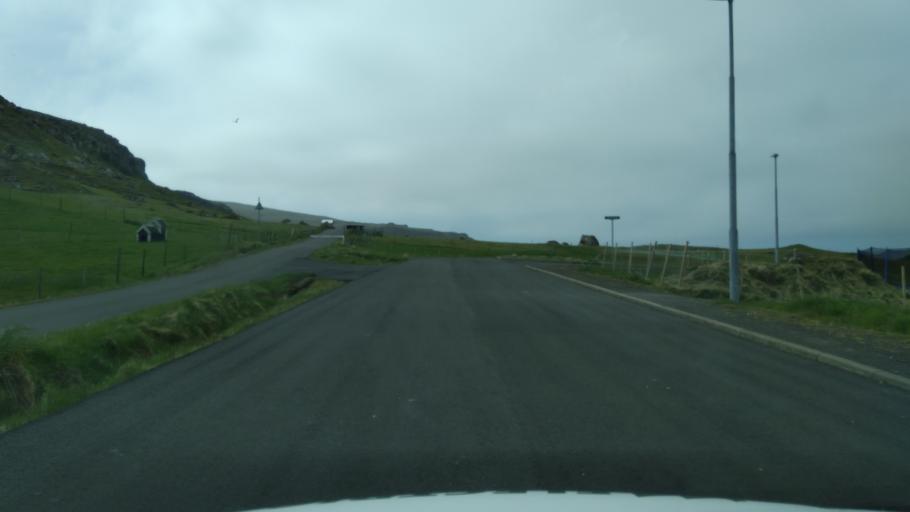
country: FO
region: Sandoy
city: Sandur
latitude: 61.9037
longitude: -6.8930
